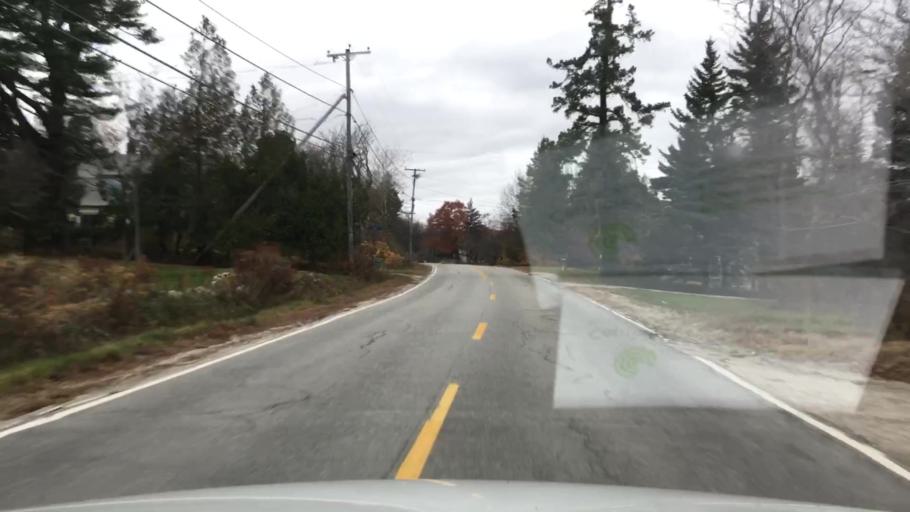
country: US
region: Maine
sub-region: Hancock County
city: Sedgwick
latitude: 44.3611
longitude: -68.5502
